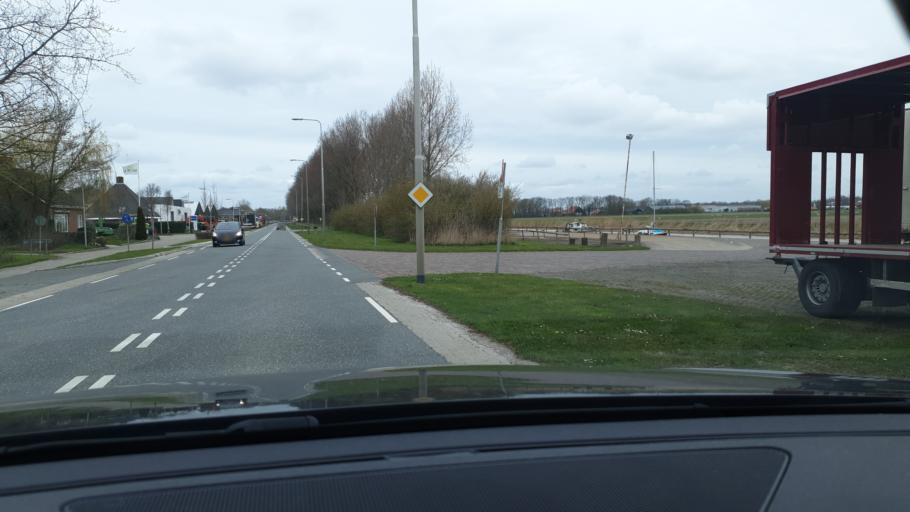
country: NL
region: Flevoland
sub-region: Gemeente Urk
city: Urk
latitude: 52.7172
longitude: 5.6455
